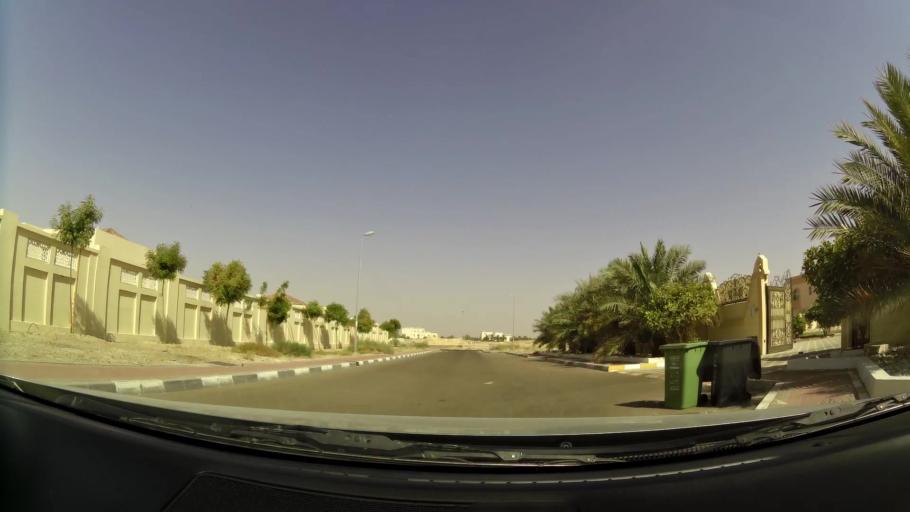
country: OM
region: Al Buraimi
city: Al Buraymi
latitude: 24.3164
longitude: 55.8109
